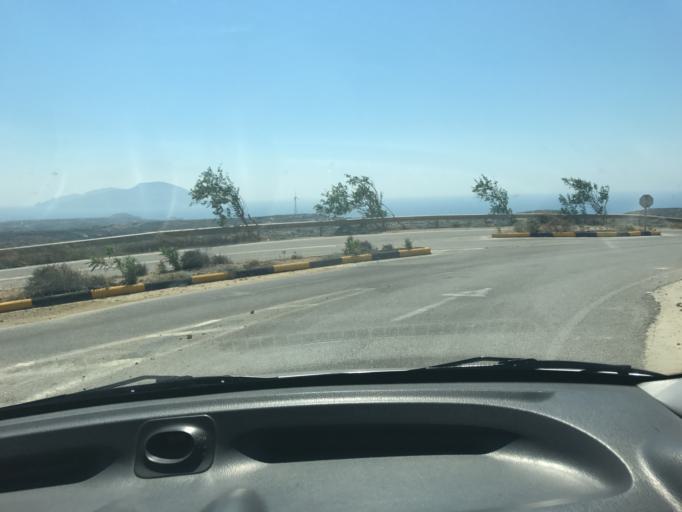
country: GR
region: South Aegean
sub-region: Nomos Dodekanisou
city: Karpathos
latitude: 35.4693
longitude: 27.1371
